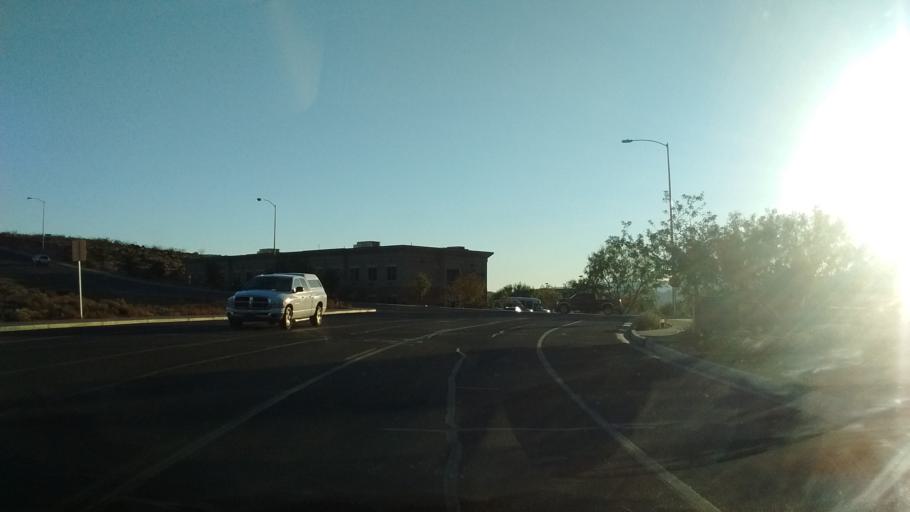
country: US
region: Utah
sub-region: Washington County
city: Saint George
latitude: 37.0961
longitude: -113.5498
